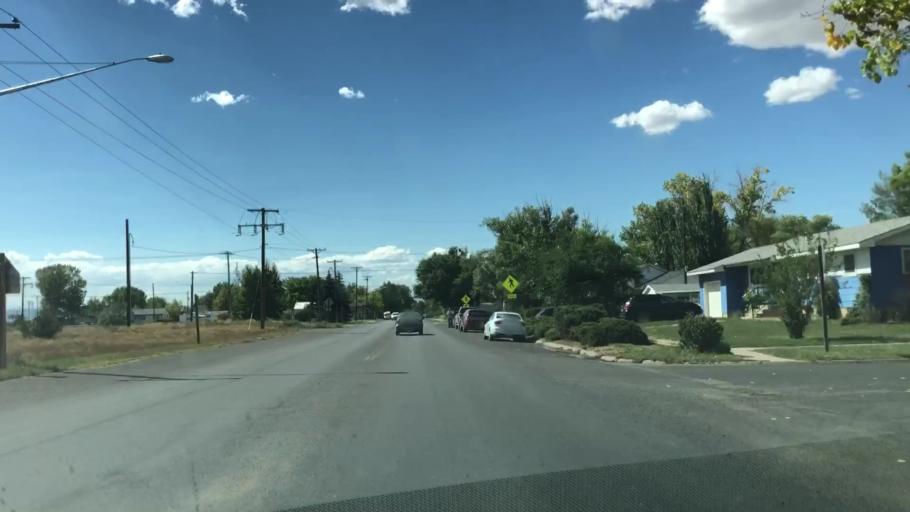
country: US
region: Wyoming
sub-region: Albany County
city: Laramie
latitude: 41.3030
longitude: -105.5851
